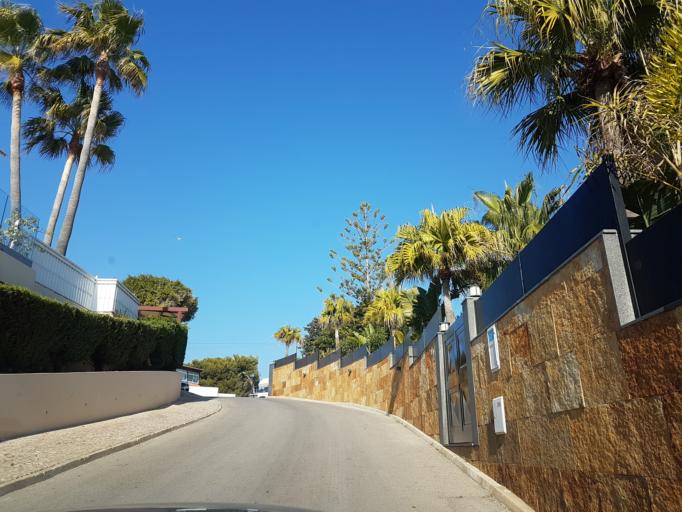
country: PT
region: Faro
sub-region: Albufeira
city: Albufeira
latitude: 37.0852
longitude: -8.2305
